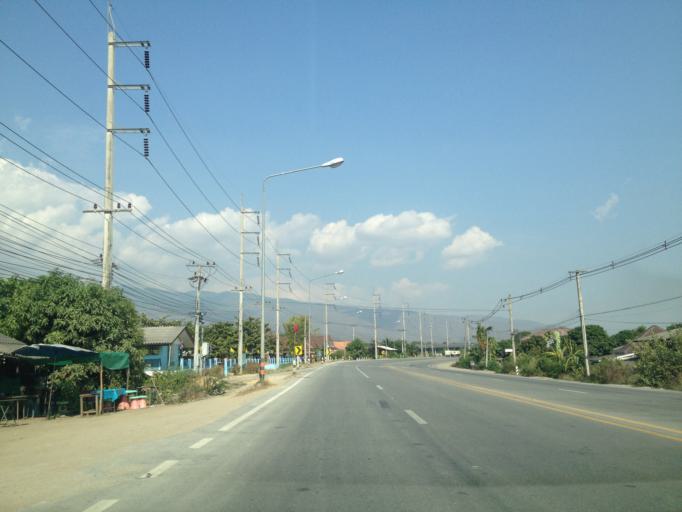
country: TH
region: Chiang Mai
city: Hot
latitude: 18.2767
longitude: 98.6377
